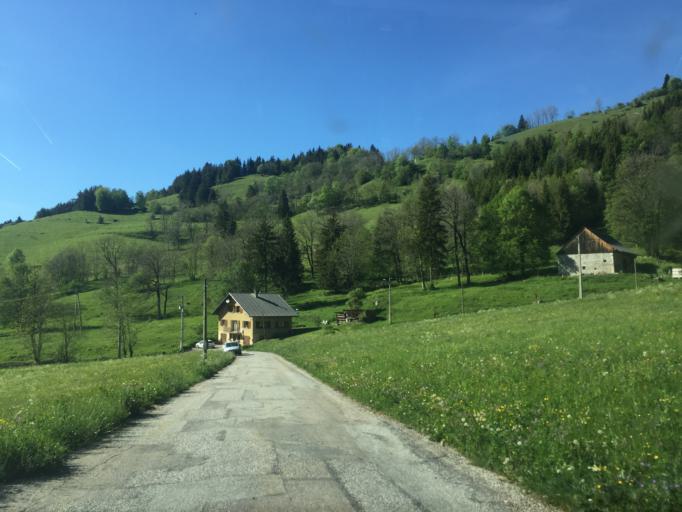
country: FR
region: Rhone-Alpes
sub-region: Departement de l'Isere
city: Barraux
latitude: 45.4432
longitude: 5.9054
